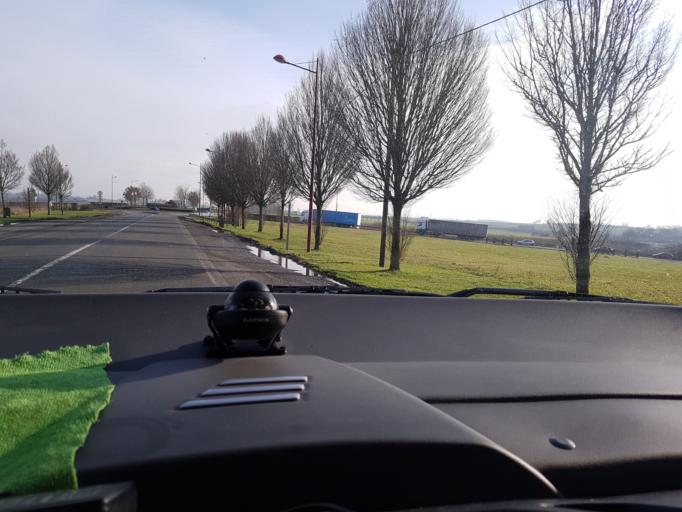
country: FR
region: Picardie
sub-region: Departement de l'Aisne
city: Hirson
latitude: 49.9060
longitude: 4.0945
